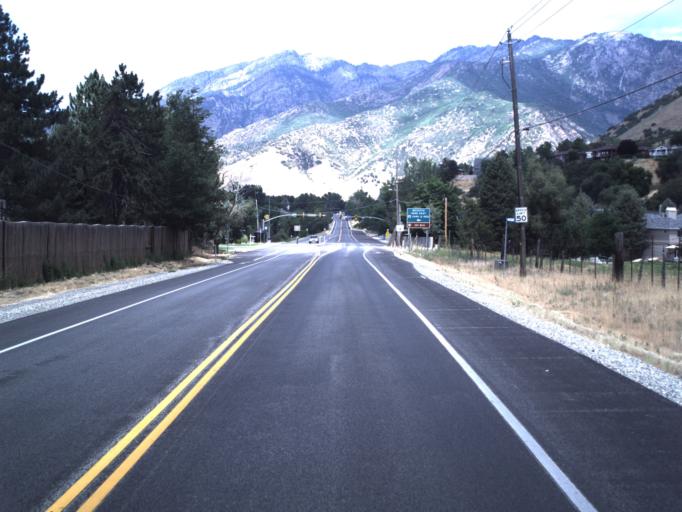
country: US
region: Utah
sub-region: Salt Lake County
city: Cottonwood Heights
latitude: 40.6011
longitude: -111.7966
